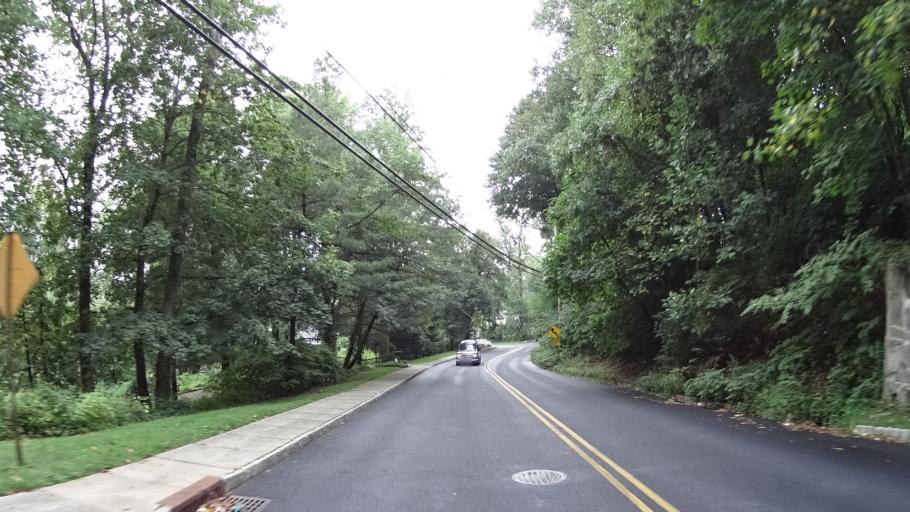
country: US
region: New Jersey
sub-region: Union County
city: Berkeley Heights
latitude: 40.7046
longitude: -74.4294
